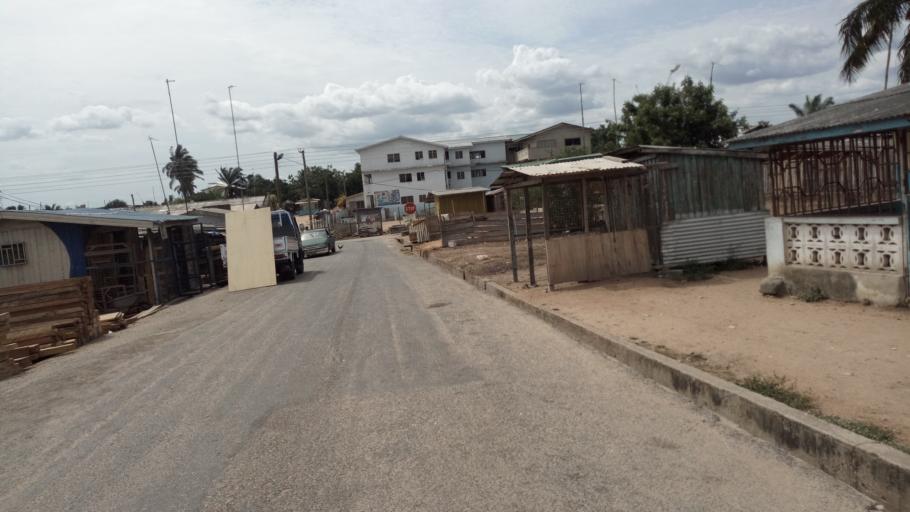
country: GH
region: Central
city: Winneba
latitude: 5.3487
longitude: -0.6245
